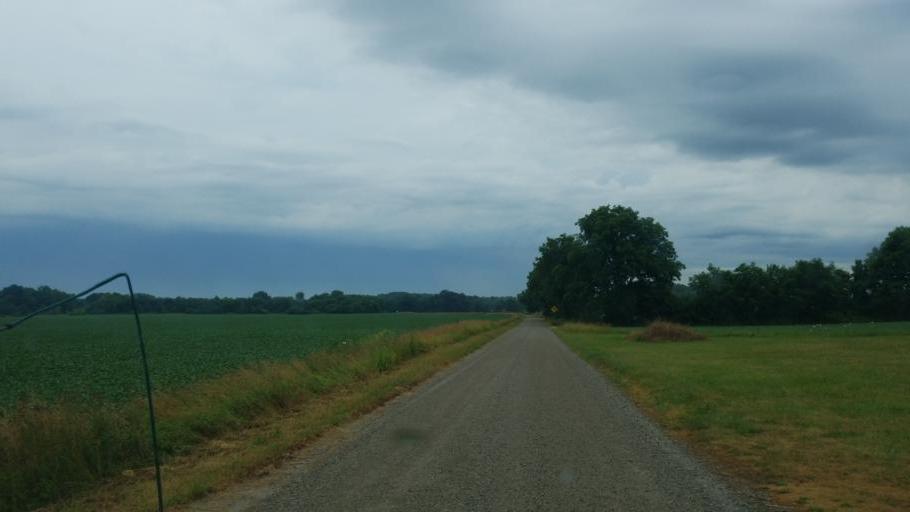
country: US
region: Indiana
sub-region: Steuben County
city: Hamilton
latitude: 41.5053
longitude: -84.9288
